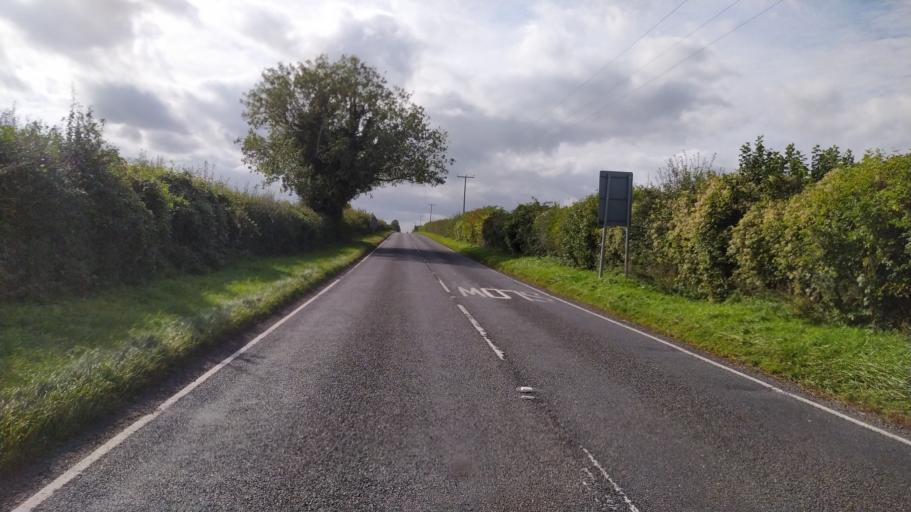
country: GB
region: England
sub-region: Hampshire
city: Winchester
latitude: 51.1404
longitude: -1.3851
